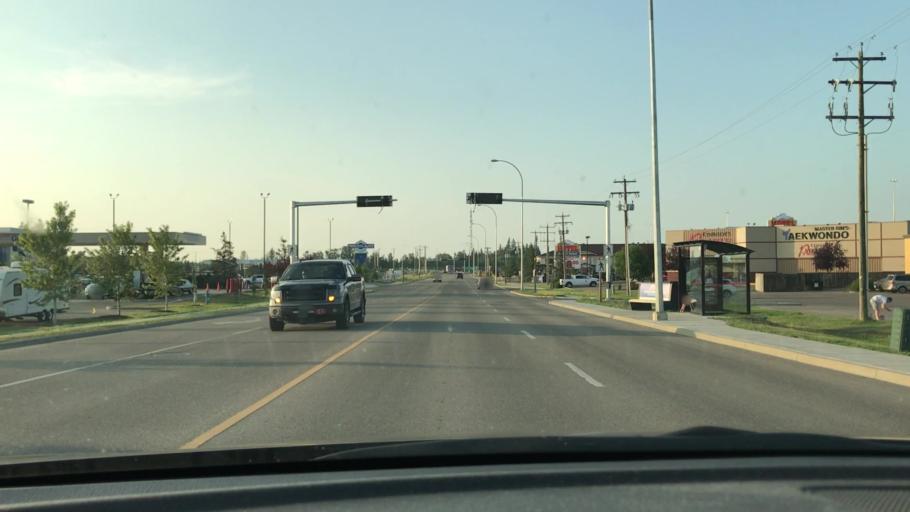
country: CA
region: Alberta
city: Red Deer
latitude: 52.2124
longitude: -113.8161
